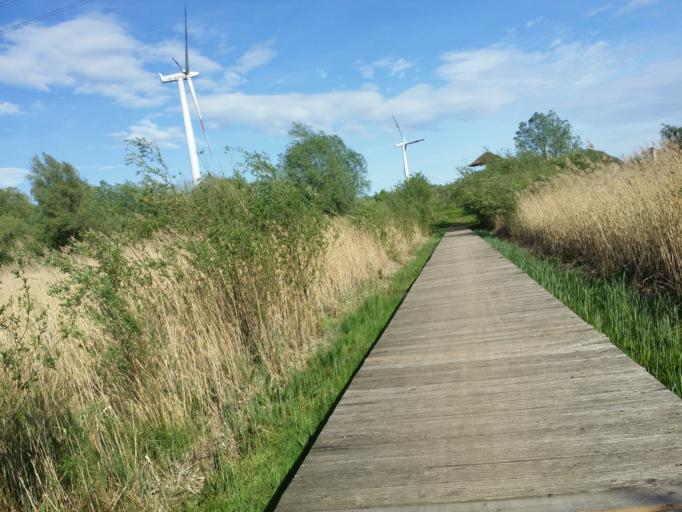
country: DE
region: Lower Saxony
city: Lemwerder
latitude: 53.1421
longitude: 8.6632
